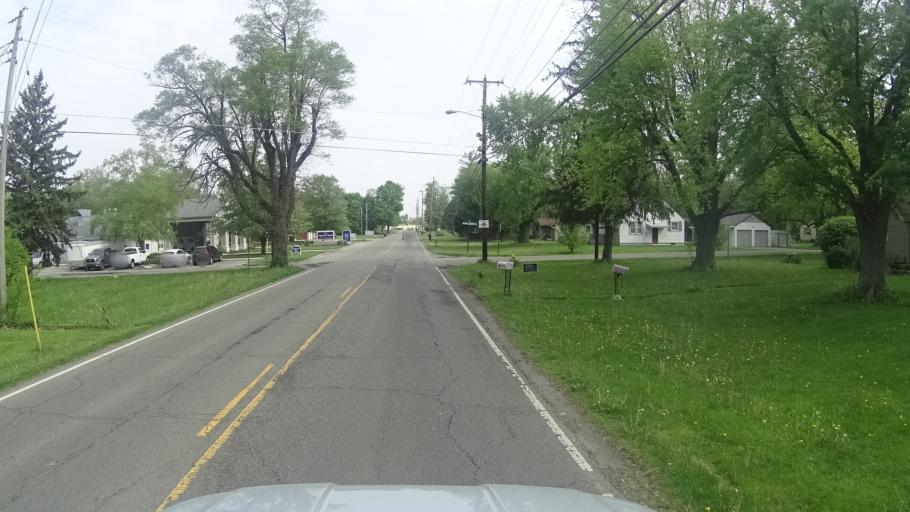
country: US
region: Indiana
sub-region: Madison County
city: Anderson
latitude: 40.1317
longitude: -85.6915
